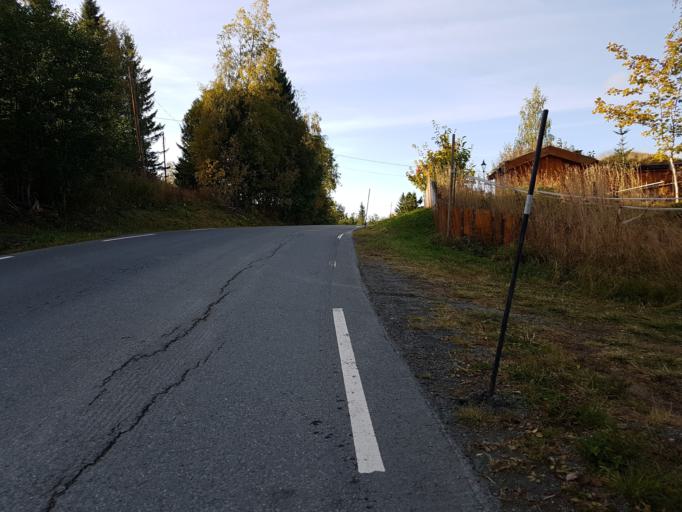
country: NO
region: Sor-Trondelag
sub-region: Klaebu
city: Klaebu
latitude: 63.3400
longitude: 10.5698
